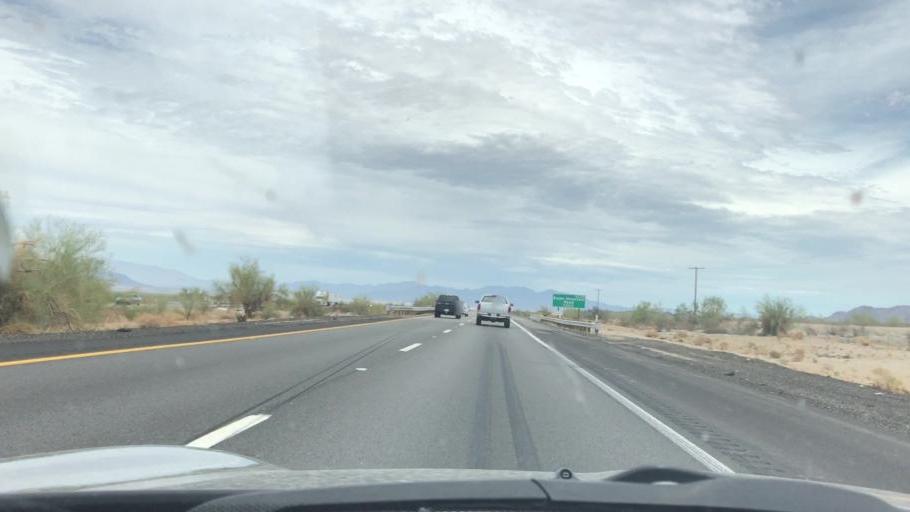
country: US
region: California
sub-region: Imperial County
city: Niland
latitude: 33.6971
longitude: -115.4761
